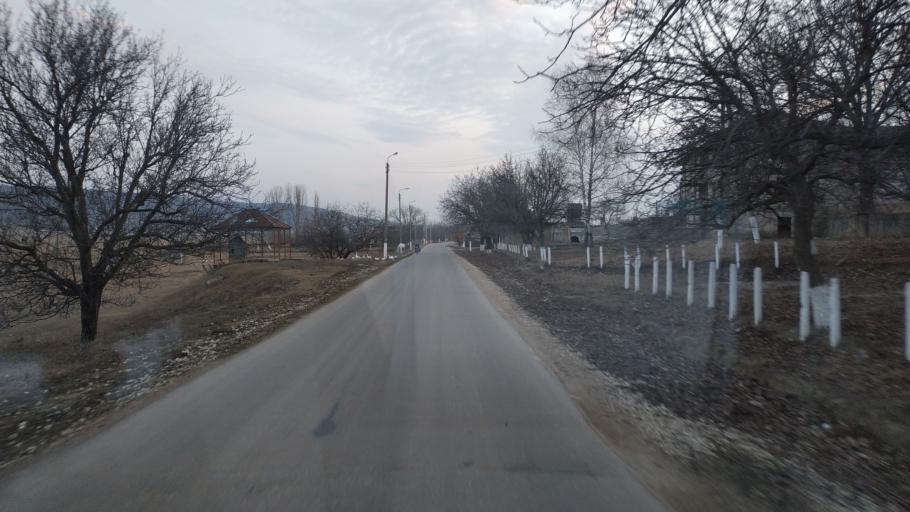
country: MD
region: Hincesti
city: Dancu
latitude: 46.6601
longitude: 28.3063
